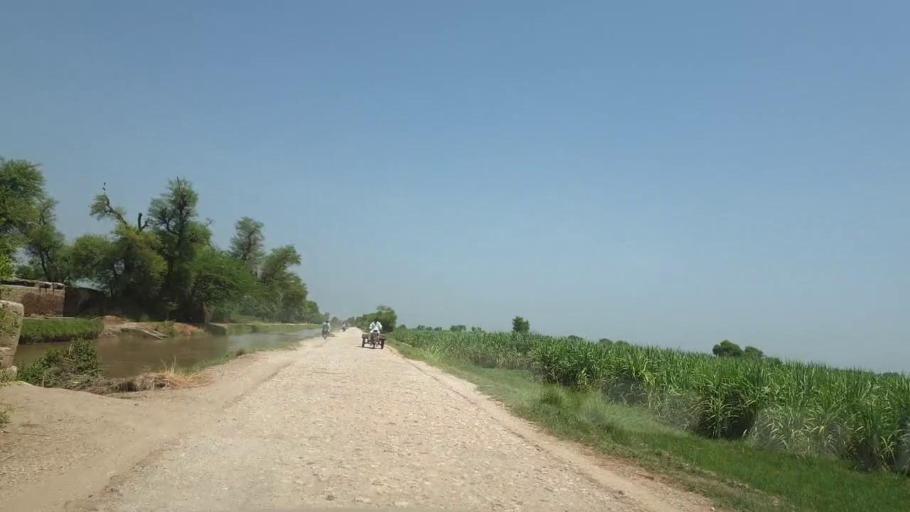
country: PK
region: Sindh
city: Pano Aqil
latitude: 27.6555
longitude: 69.1067
